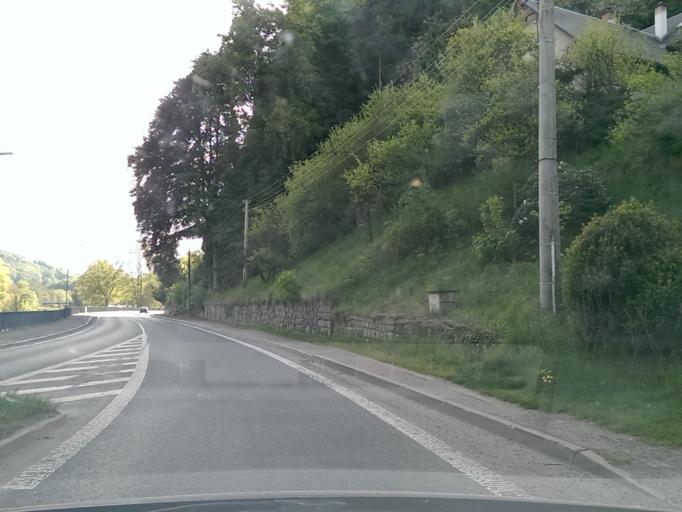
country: CZ
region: Liberecky
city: Mala Skala
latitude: 50.6423
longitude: 15.1930
